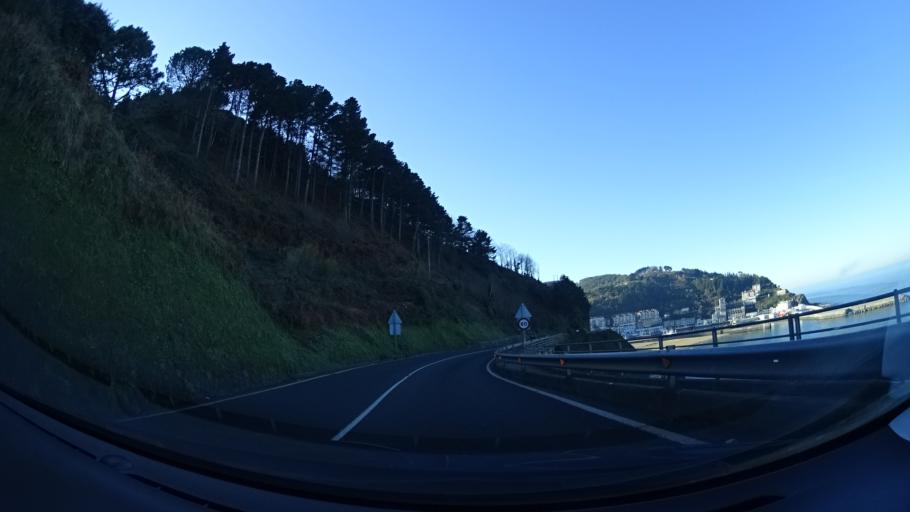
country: ES
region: Basque Country
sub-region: Bizkaia
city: Ondarroa
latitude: 43.3206
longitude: -2.4130
